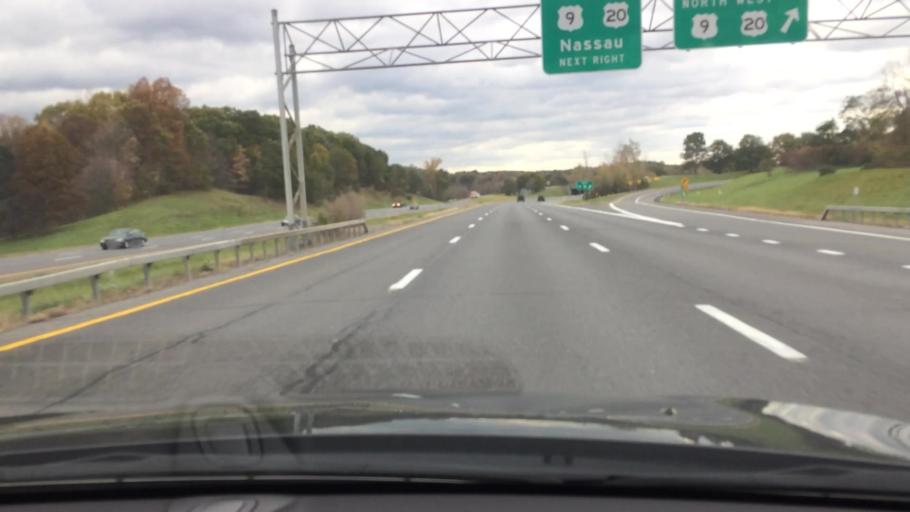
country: US
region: New York
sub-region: Rensselaer County
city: East Greenbush
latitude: 42.5637
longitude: -73.6789
